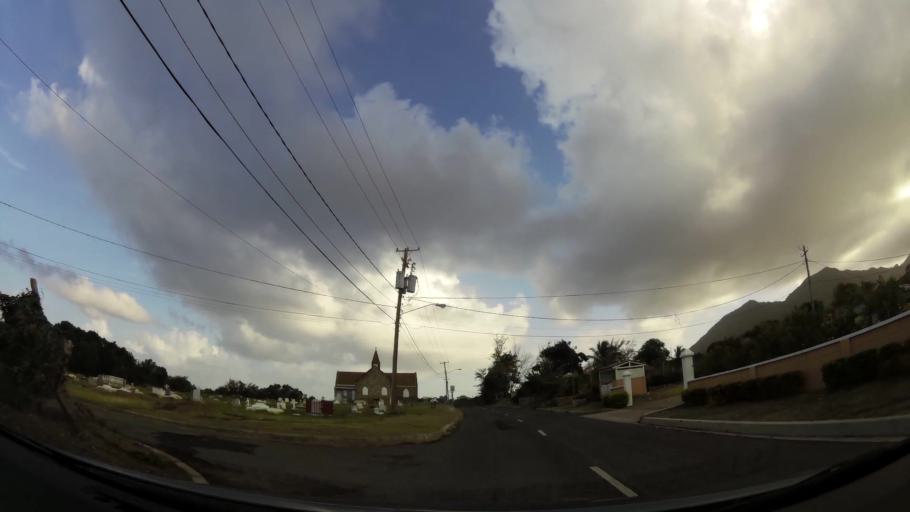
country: KN
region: Saint James Windwa
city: Newcastle
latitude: 17.1901
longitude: -62.5620
